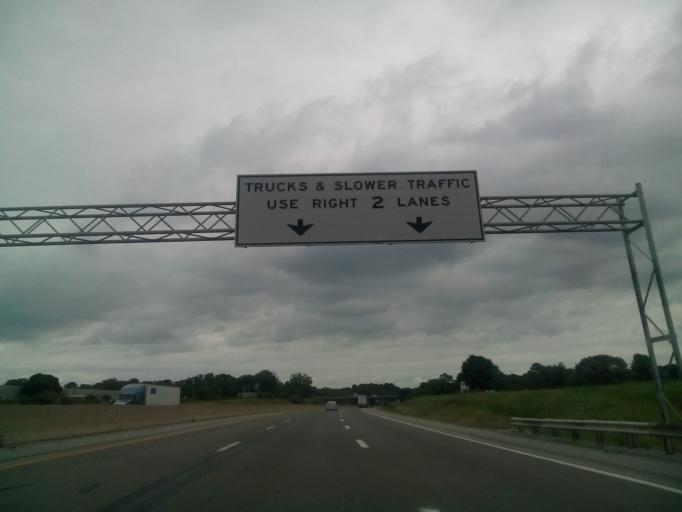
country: US
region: Ohio
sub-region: Erie County
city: Milan
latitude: 41.3244
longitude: -82.5996
